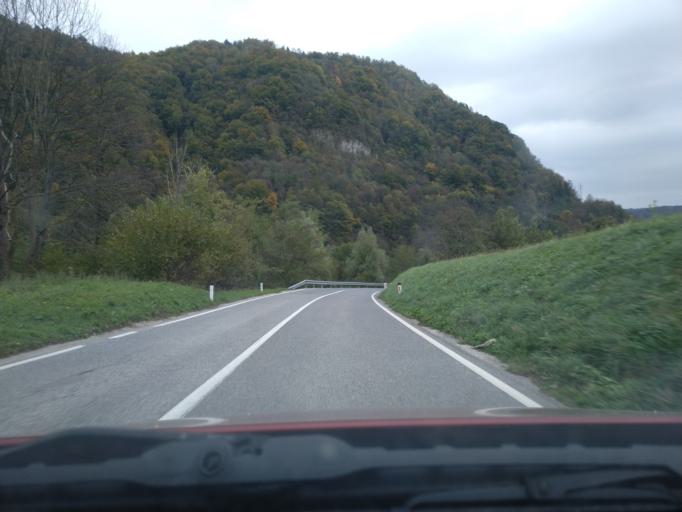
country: SI
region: Tolmin
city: Tolmin
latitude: 46.1566
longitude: 13.7161
